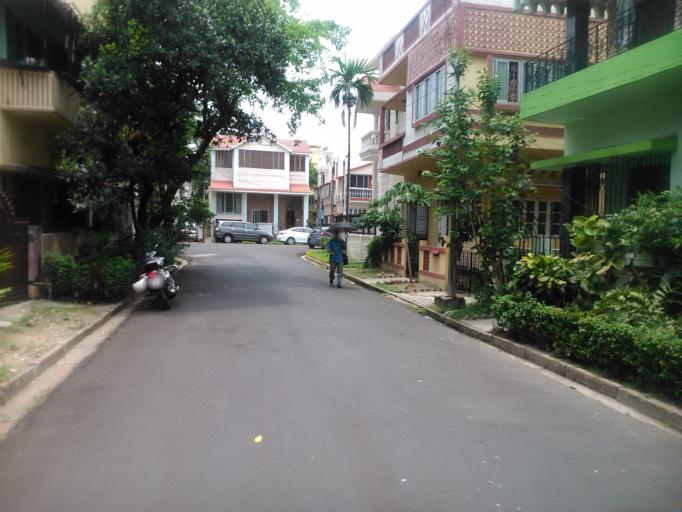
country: IN
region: West Bengal
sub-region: North 24 Parganas
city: Garui
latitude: 22.5934
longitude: 88.4068
